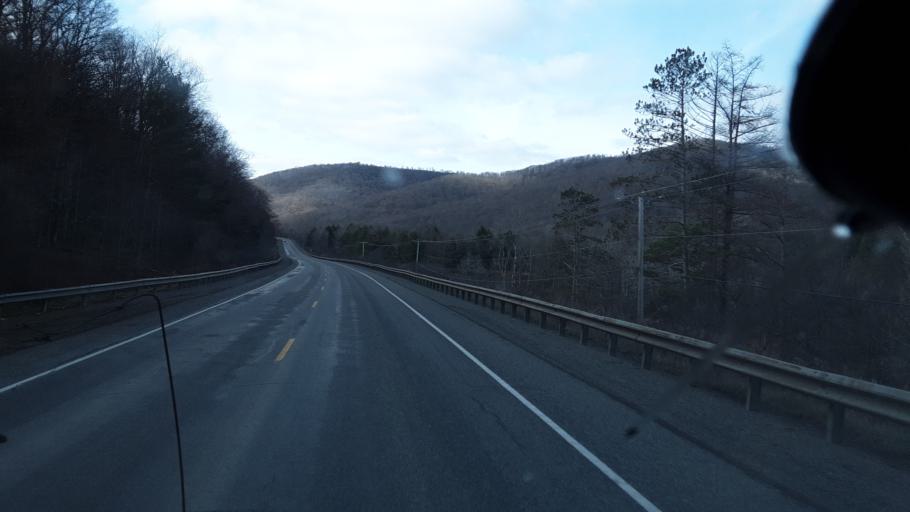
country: US
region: Pennsylvania
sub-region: Potter County
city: Galeton
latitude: 41.7897
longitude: -77.7778
